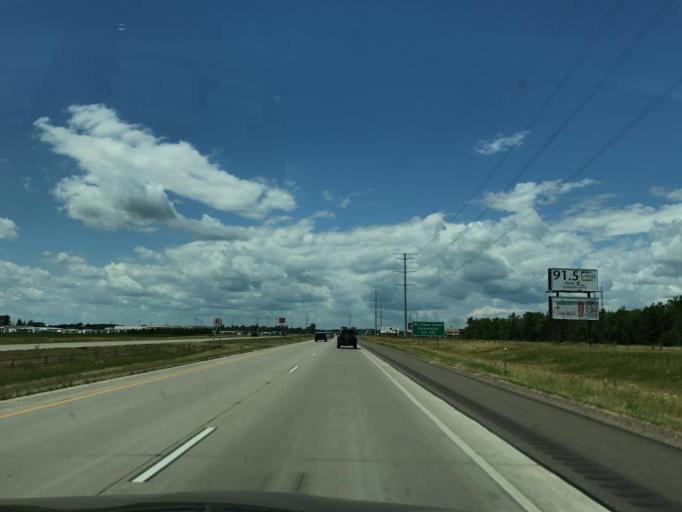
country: US
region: Minnesota
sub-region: Stearns County
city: Saint Augusta
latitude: 45.4825
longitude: -94.1430
